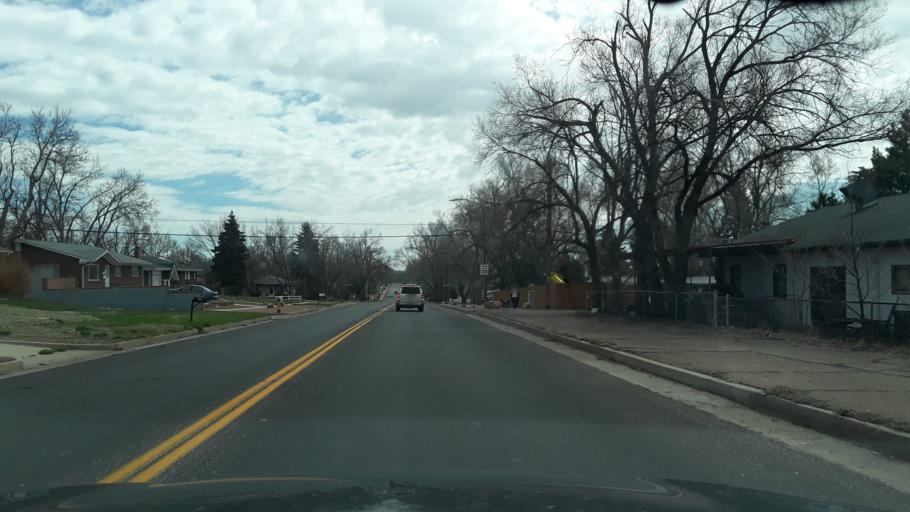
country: US
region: Colorado
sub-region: El Paso County
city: Colorado Springs
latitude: 38.8489
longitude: -104.7872
